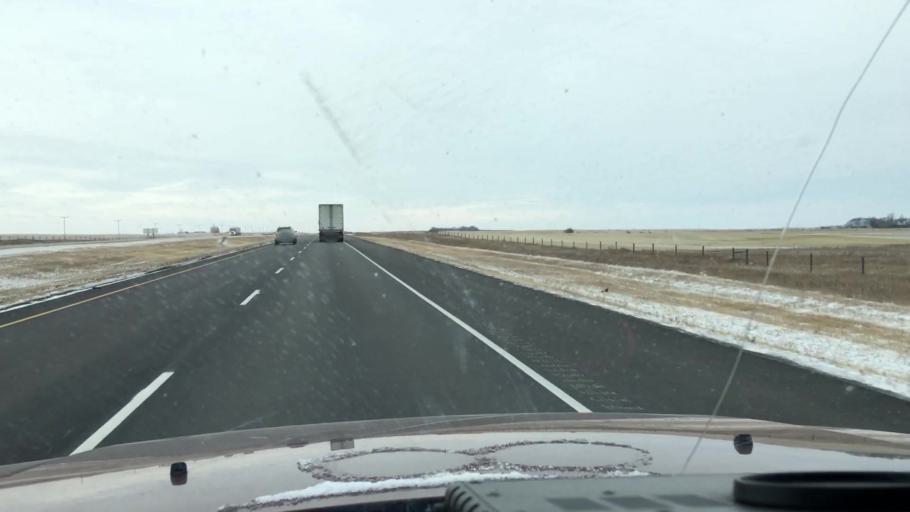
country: CA
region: Saskatchewan
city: Saskatoon
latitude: 51.8008
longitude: -106.4899
